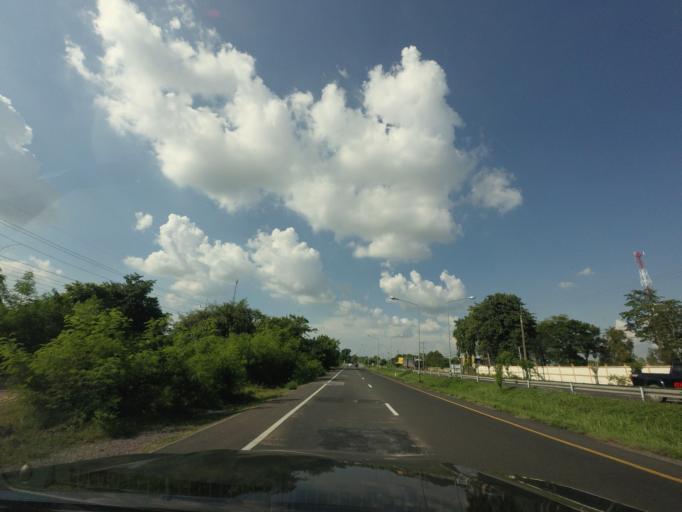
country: TH
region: Nakhon Ratchasima
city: Bua Lai
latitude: 15.6796
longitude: 102.5768
